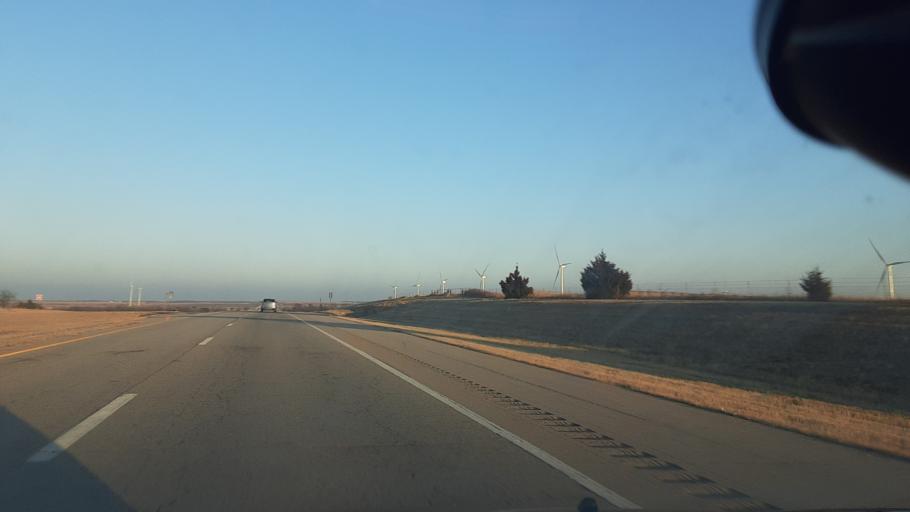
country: US
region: Oklahoma
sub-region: Noble County
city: Perry
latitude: 36.3978
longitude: -97.4366
